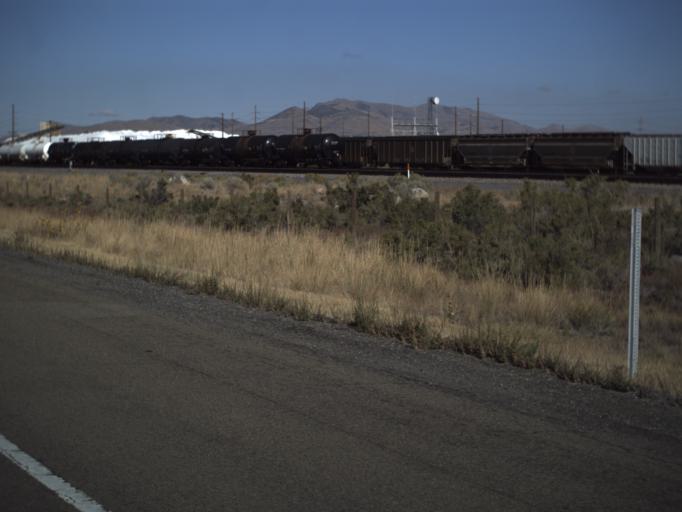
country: US
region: Utah
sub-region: Tooele County
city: Grantsville
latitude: 40.7458
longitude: -112.6484
